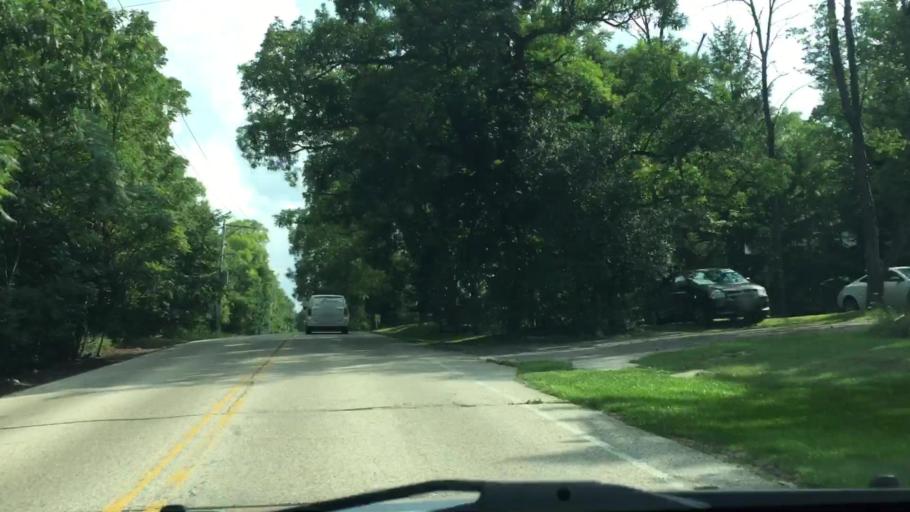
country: US
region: Wisconsin
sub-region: Waukesha County
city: Wales
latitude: 43.0433
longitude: -88.3496
